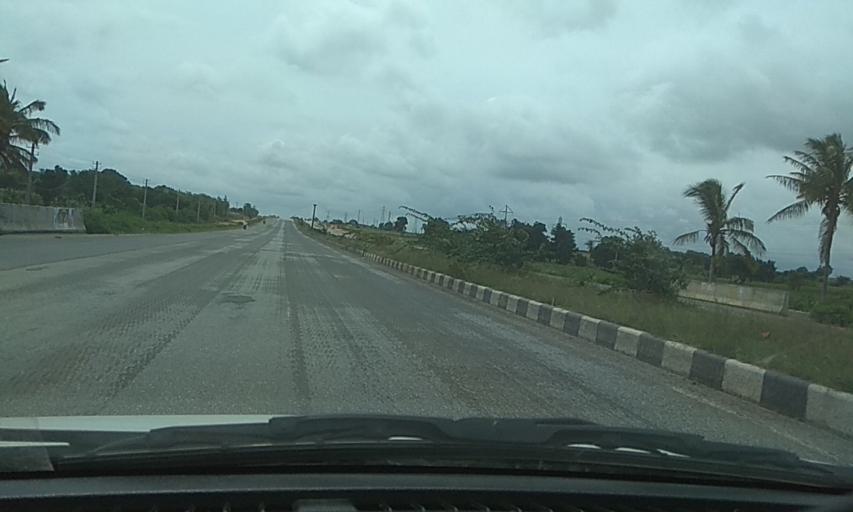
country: IN
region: Karnataka
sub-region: Davanagere
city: Mayakonda
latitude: 14.3321
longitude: 76.2186
